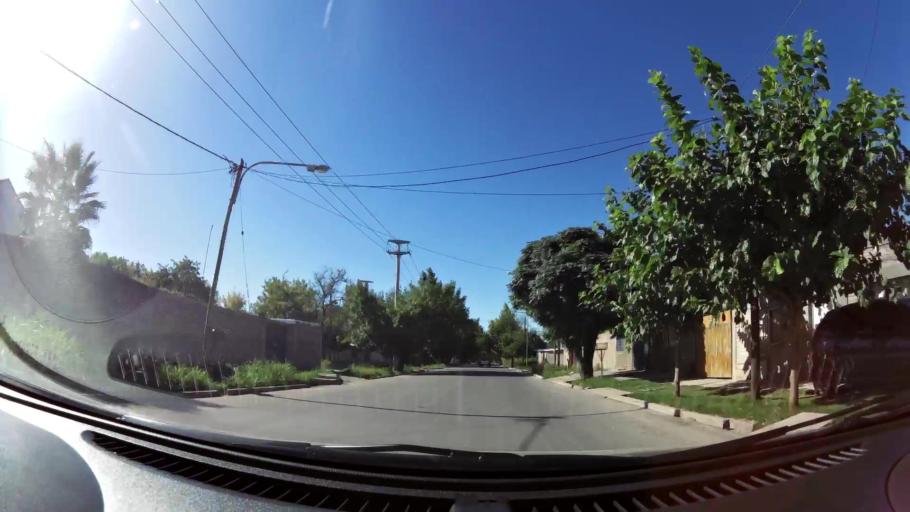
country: AR
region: Mendoza
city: Las Heras
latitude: -32.8357
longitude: -68.8295
